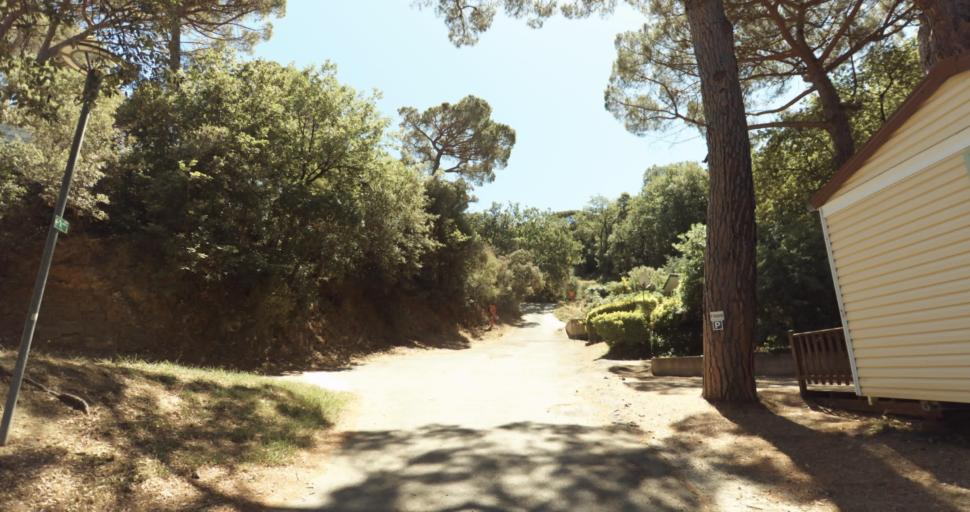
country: FR
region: Provence-Alpes-Cote d'Azur
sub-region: Departement du Var
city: Gassin
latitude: 43.2417
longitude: 6.5768
